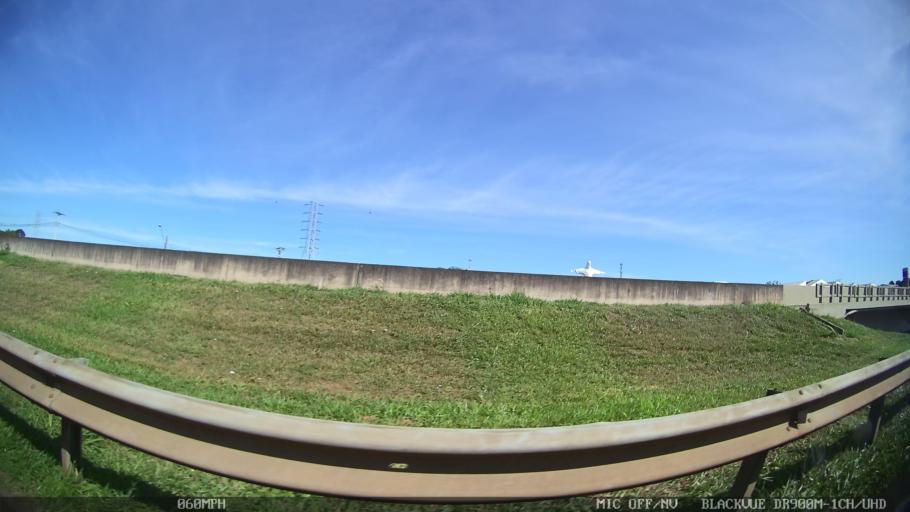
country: BR
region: Sao Paulo
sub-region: Pirassununga
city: Pirassununga
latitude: -21.9988
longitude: -47.4455
